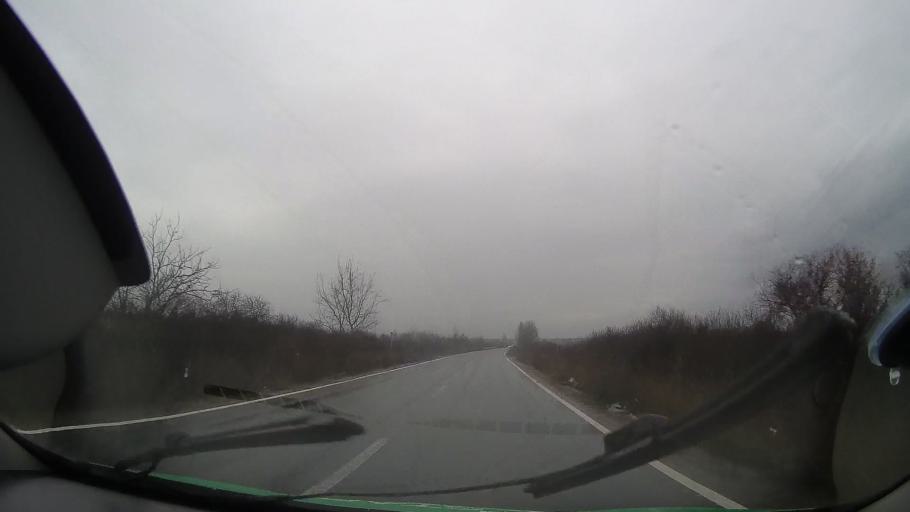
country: RO
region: Bihor
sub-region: Comuna Tinca
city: Tinca
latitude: 46.7430
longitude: 21.9396
